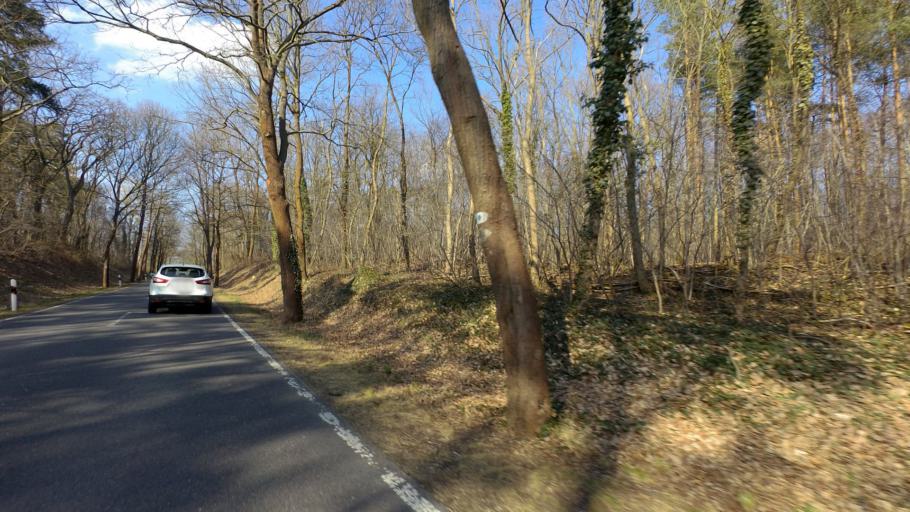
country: DE
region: Brandenburg
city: Trebbin
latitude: 52.2304
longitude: 13.1375
